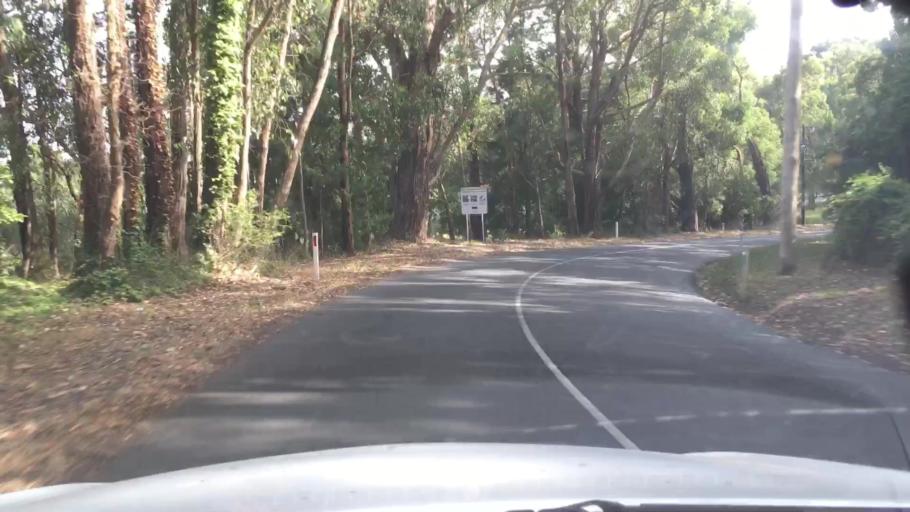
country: AU
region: Victoria
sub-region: Yarra Ranges
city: Macclesfield
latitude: -37.8927
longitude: 145.4752
